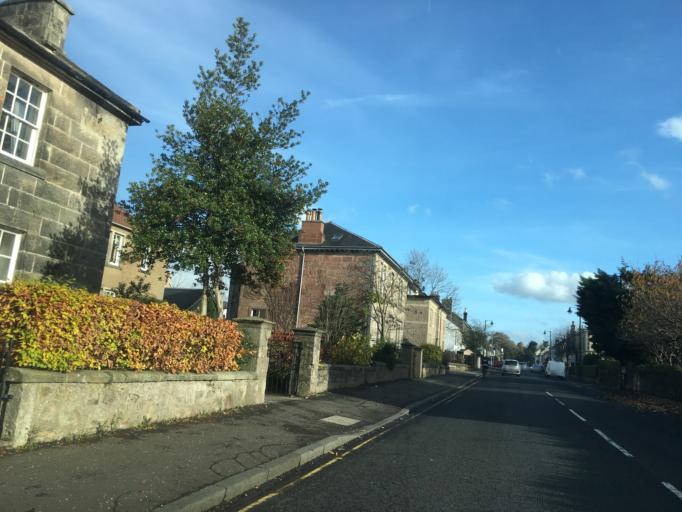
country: GB
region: Scotland
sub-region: Clackmannanshire
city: Dollar
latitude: 56.1625
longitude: -3.6769
